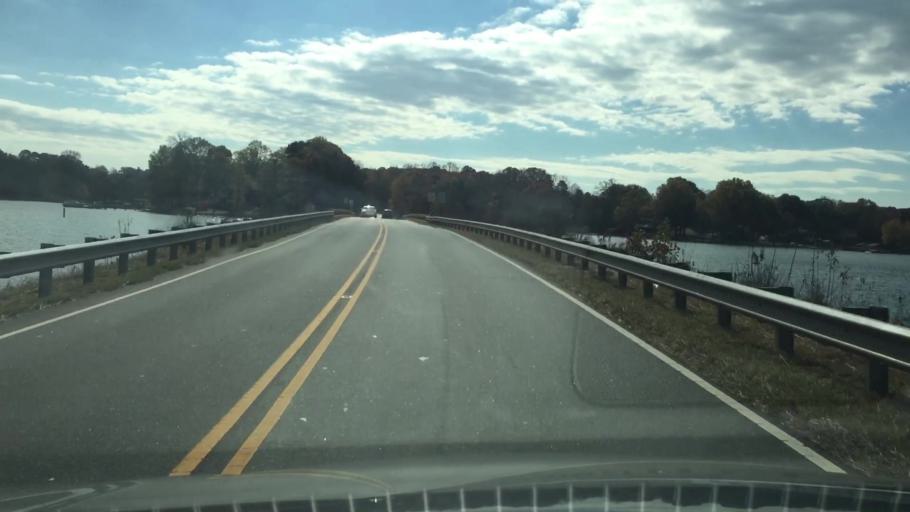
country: US
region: North Carolina
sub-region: Iredell County
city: Mooresville
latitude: 35.5652
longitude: -80.8662
